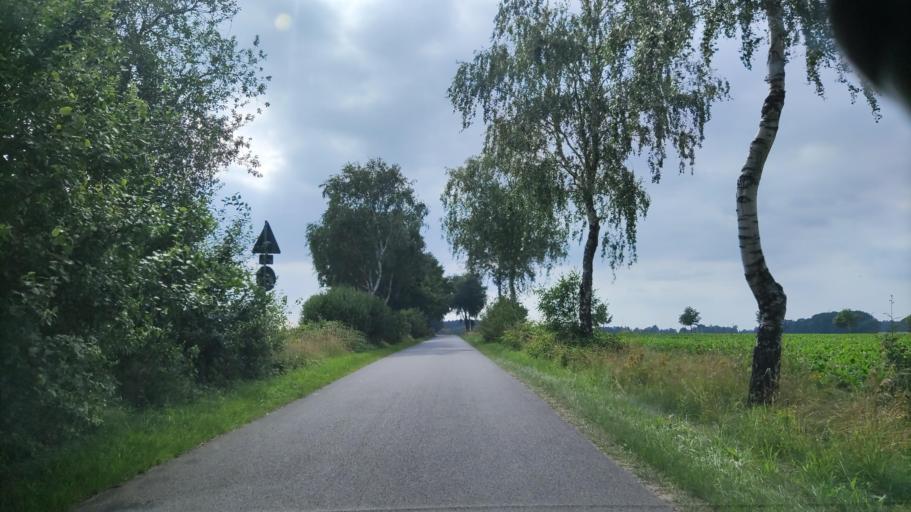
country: DE
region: Lower Saxony
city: Schneverdingen
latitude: 53.0662
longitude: 9.8195
